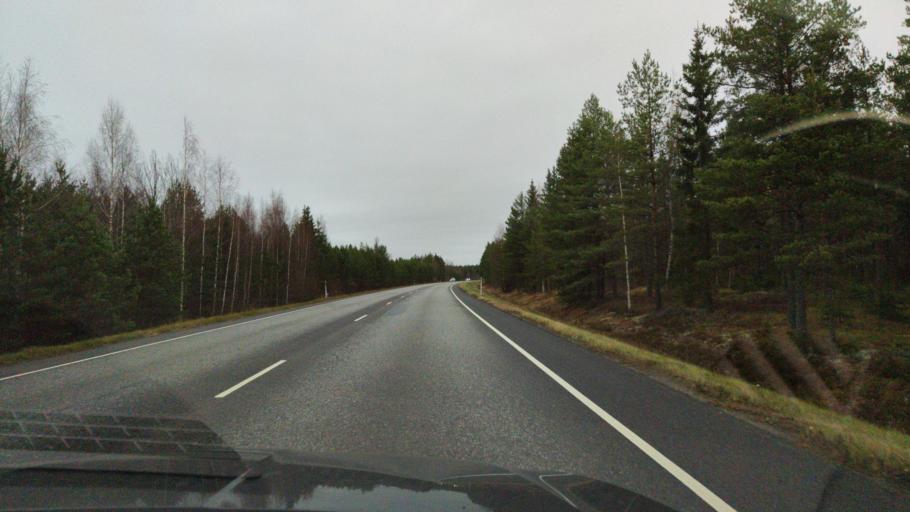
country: FI
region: Varsinais-Suomi
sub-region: Loimaa
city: Ylaene
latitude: 60.9722
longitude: 22.4109
